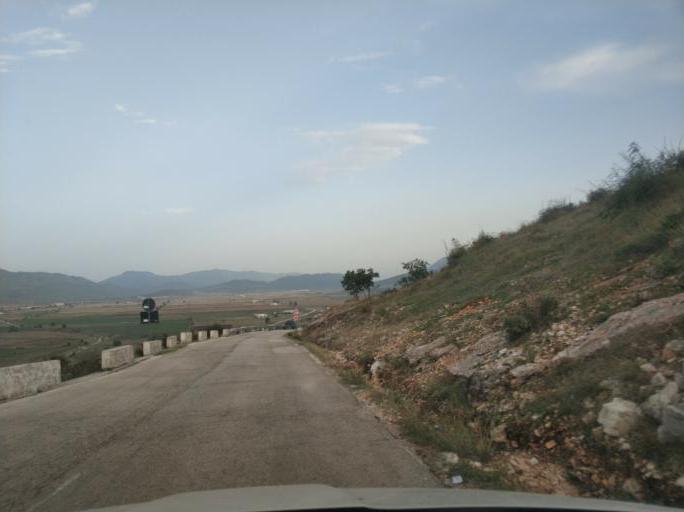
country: AL
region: Gjirokaster
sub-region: Rrethi i Gjirokastres
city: Libohove
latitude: 39.9465
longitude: 20.2553
